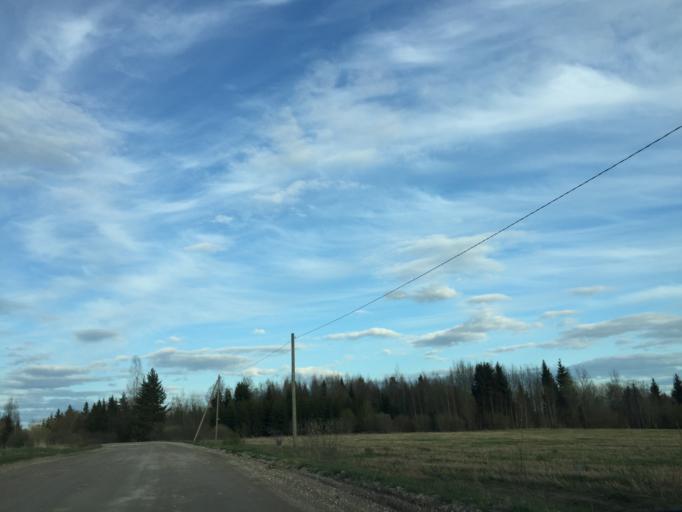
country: LV
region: Rezekne
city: Rezekne
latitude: 56.5749
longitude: 27.3430
